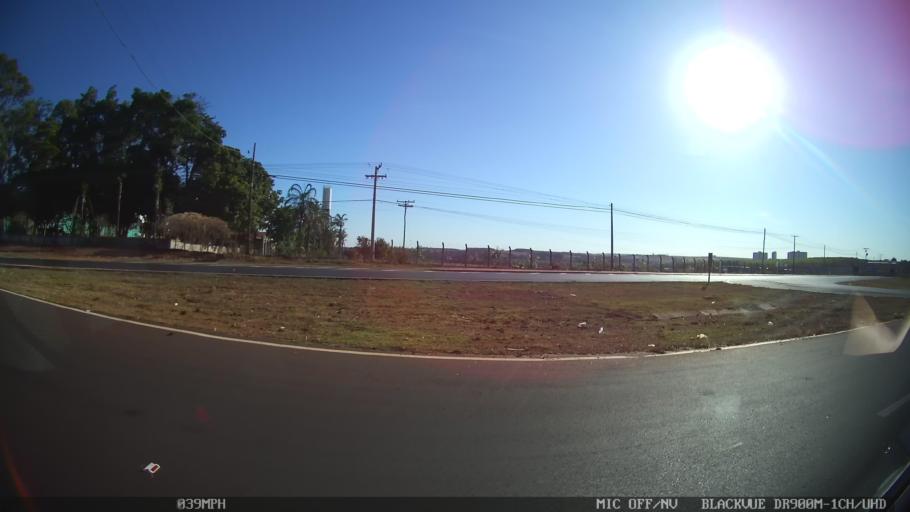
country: BR
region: Sao Paulo
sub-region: Olimpia
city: Olimpia
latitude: -20.7121
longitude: -48.9093
